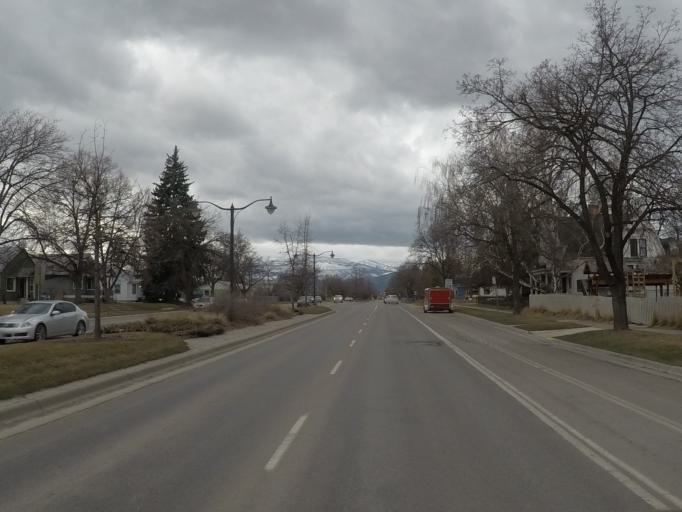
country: US
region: Montana
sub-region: Missoula County
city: Missoula
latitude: 46.8607
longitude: -114.0073
